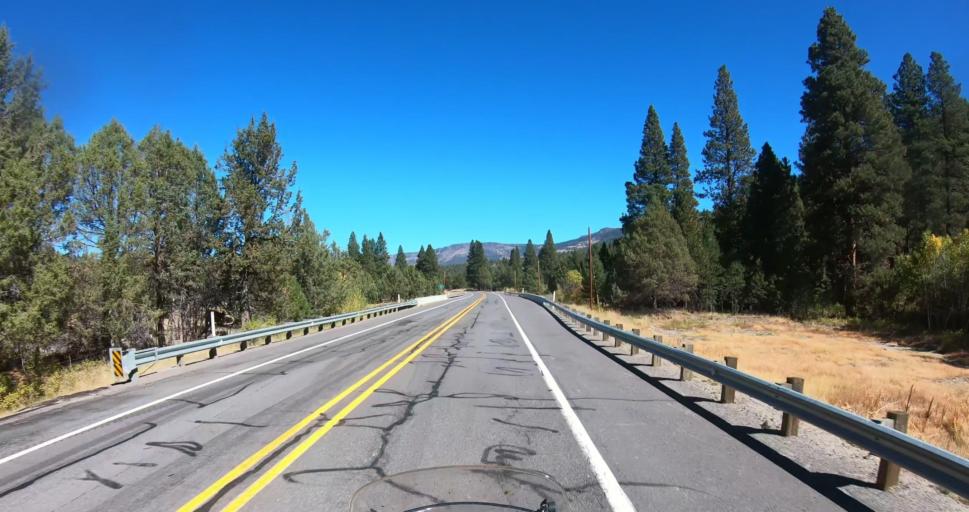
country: US
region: Oregon
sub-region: Lake County
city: Lakeview
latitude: 42.3955
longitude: -120.2967
